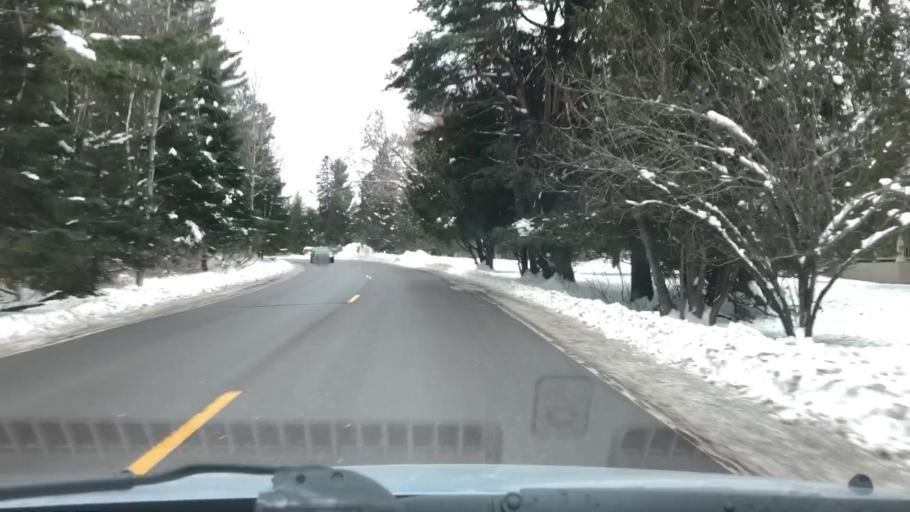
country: US
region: Minnesota
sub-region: Carlton County
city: Carlton
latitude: 46.6647
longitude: -92.4150
